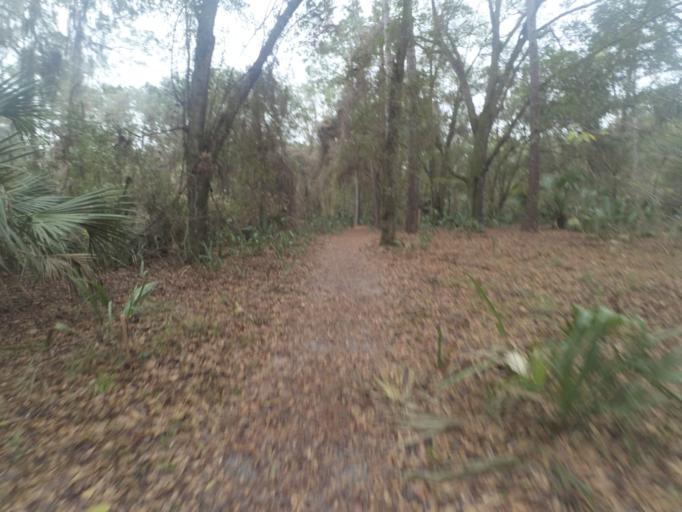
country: US
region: Florida
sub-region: Alachua County
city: Gainesville
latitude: 29.5487
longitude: -82.2939
